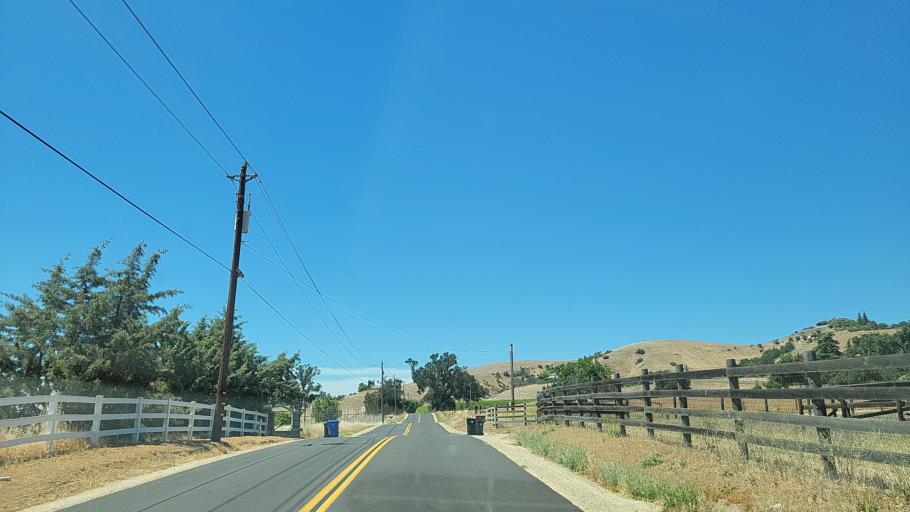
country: US
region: California
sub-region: San Luis Obispo County
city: Atascadero
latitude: 35.4832
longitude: -120.6314
